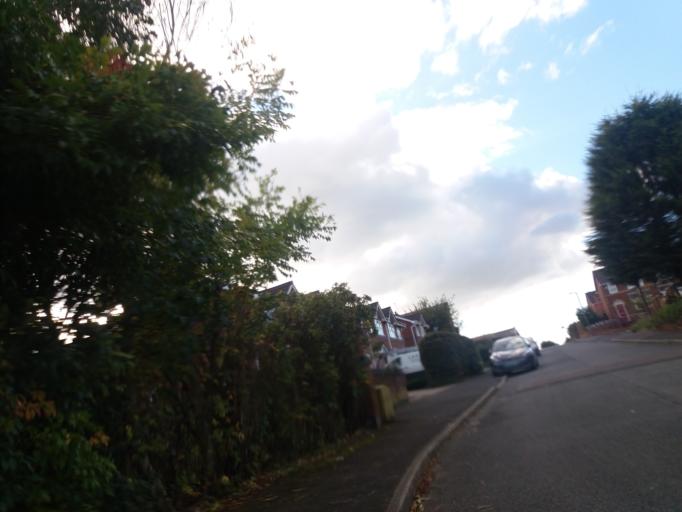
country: GB
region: England
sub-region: Lancashire
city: Chorley
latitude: 53.6545
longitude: -2.6160
